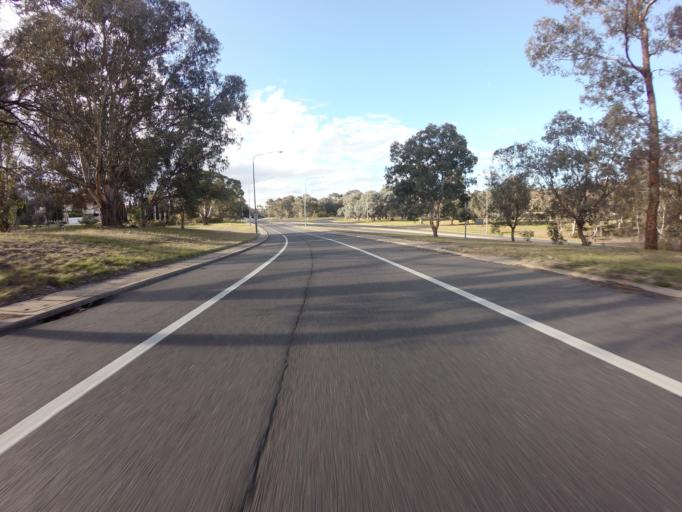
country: AU
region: Australian Capital Territory
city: Forrest
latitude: -35.3087
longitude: 149.1189
